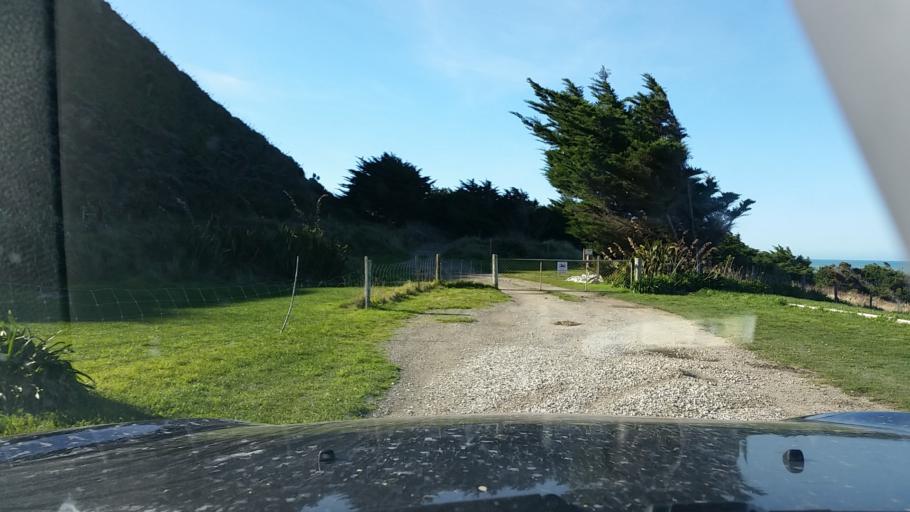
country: NZ
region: Marlborough
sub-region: Marlborough District
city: Blenheim
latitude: -41.8439
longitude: 174.1835
